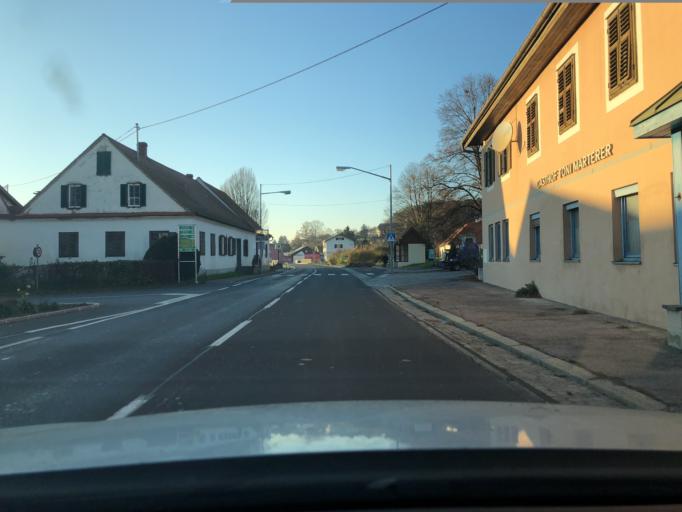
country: AT
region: Styria
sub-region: Politischer Bezirk Hartberg-Fuerstenfeld
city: Nestelbach im Ilztal
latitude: 47.0913
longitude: 15.8823
